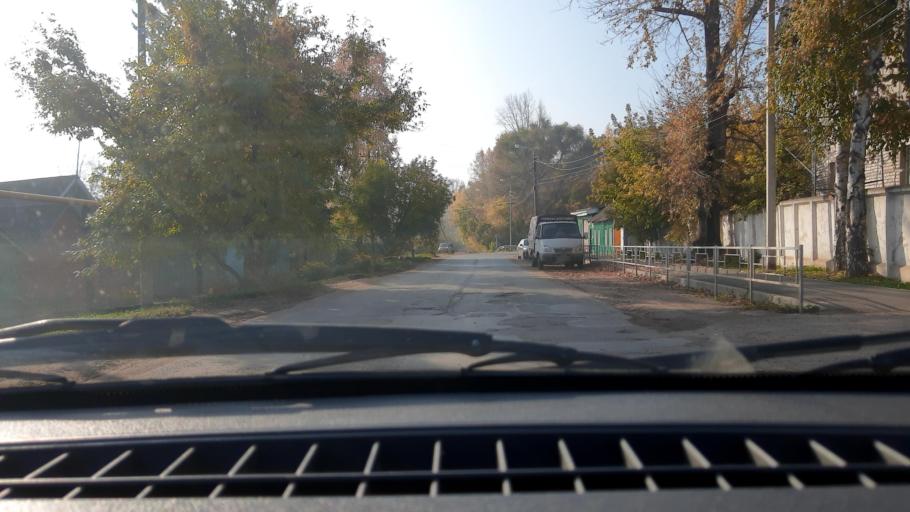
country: RU
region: Bashkortostan
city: Mikhaylovka
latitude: 54.6929
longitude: 55.8493
